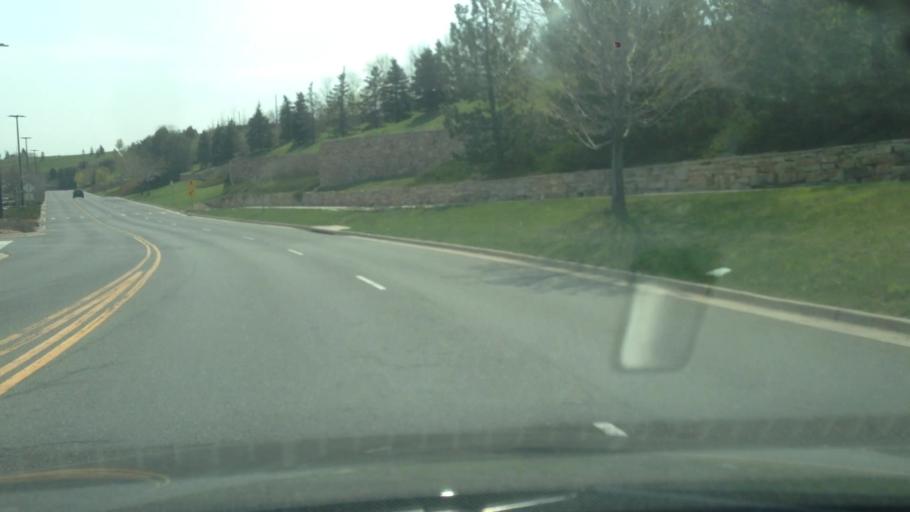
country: US
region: Colorado
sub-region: Jefferson County
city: West Pleasant View
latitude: 39.7295
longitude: -105.1626
